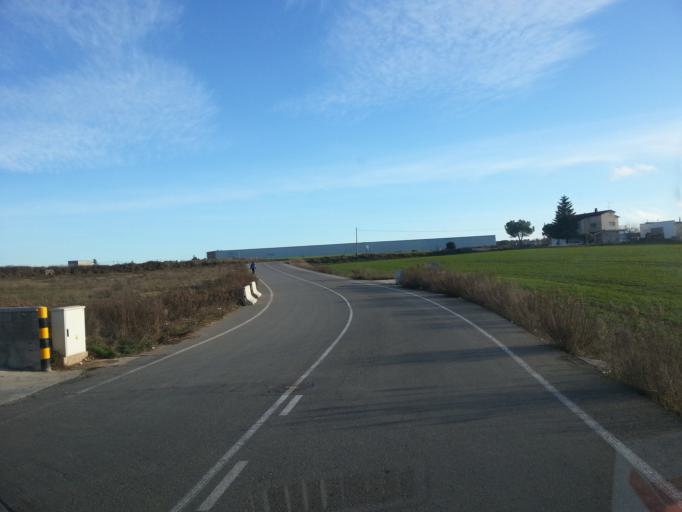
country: ES
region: Catalonia
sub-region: Provincia de Lleida
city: Olius
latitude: 41.9853
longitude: 1.5495
